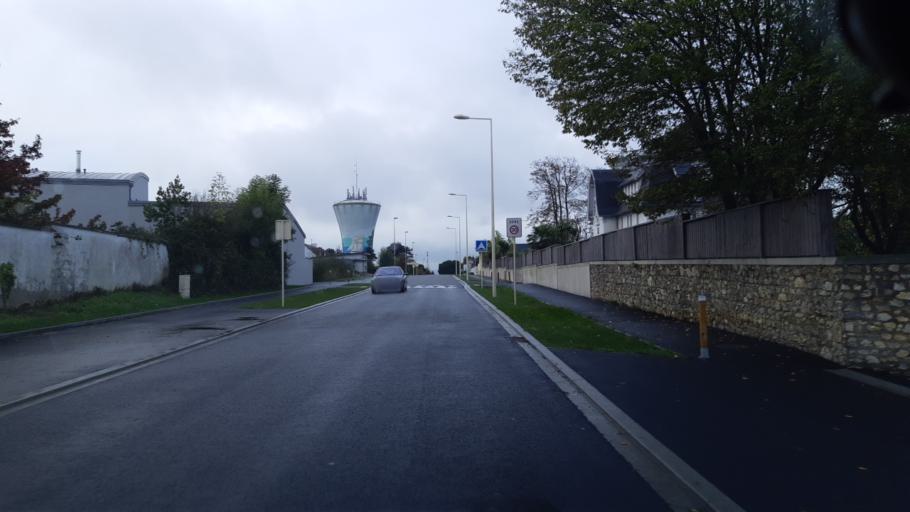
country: FR
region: Lower Normandy
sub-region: Departement de la Manche
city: Donville-les-Bains
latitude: 48.8556
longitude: -1.5620
